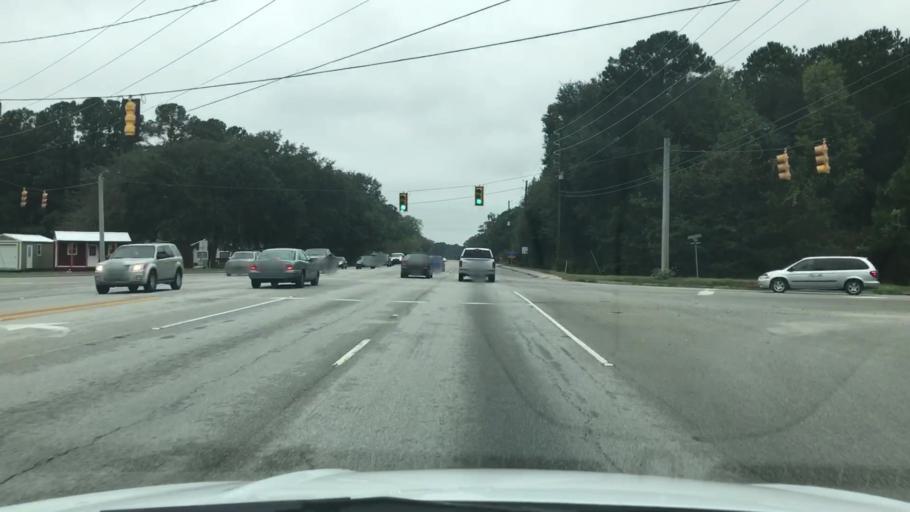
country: US
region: South Carolina
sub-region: Beaufort County
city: Shell Point
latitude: 32.4104
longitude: -80.7527
